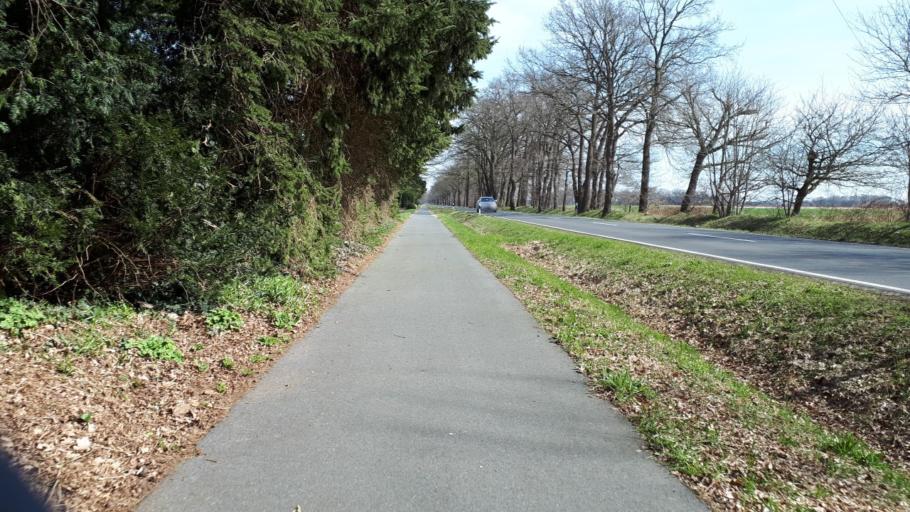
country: DE
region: Lower Saxony
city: Garrel
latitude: 52.9736
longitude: 8.0572
